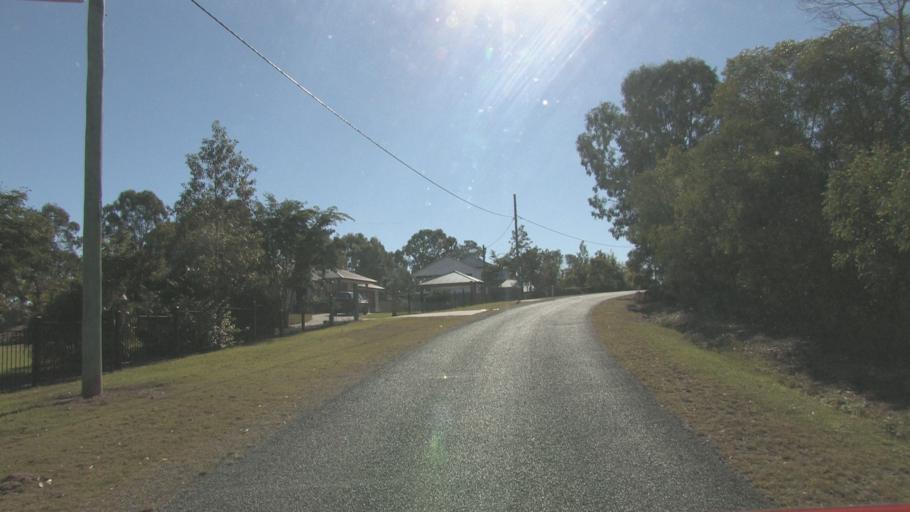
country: AU
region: Queensland
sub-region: Logan
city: Logan Reserve
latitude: -27.7447
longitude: 153.1239
